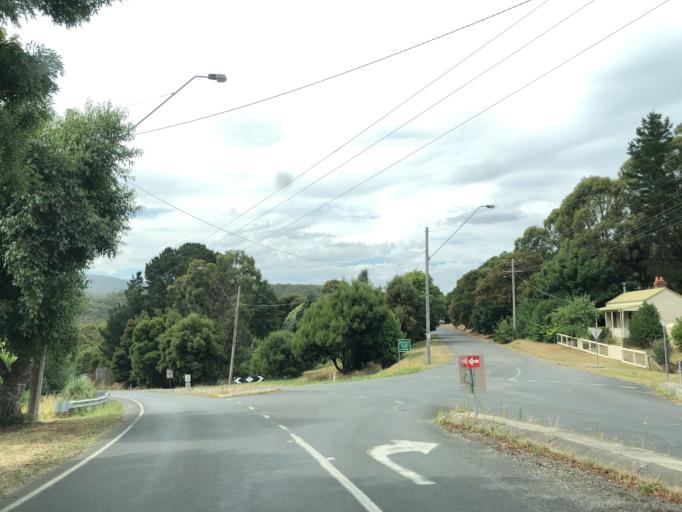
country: AU
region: Victoria
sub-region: Moorabool
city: Bacchus Marsh
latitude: -37.4724
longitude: 144.3063
